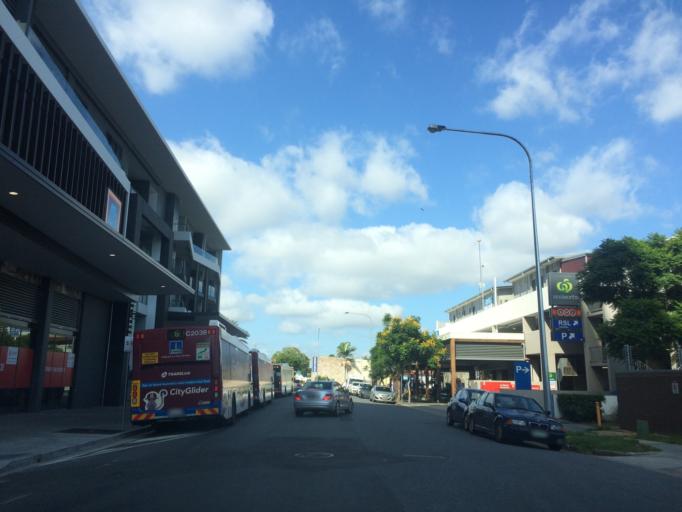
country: AU
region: Queensland
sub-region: Brisbane
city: Greenslopes
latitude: -27.4940
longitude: 153.0581
